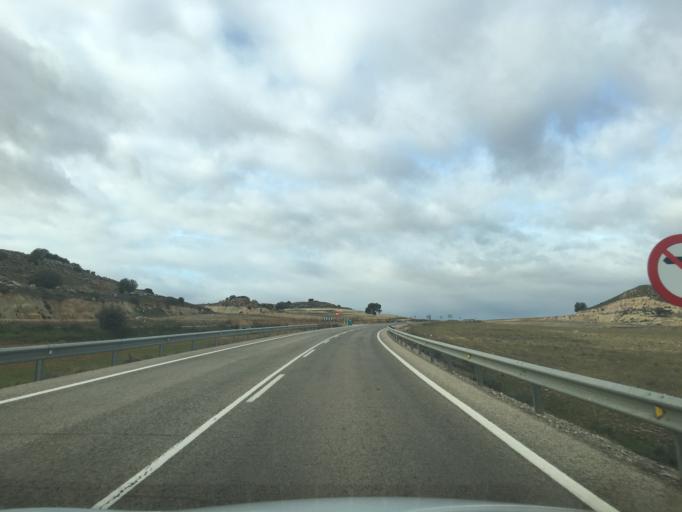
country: ES
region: Castille-La Mancha
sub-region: Provincia de Albacete
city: Petrola
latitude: 38.8270
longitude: -1.5675
